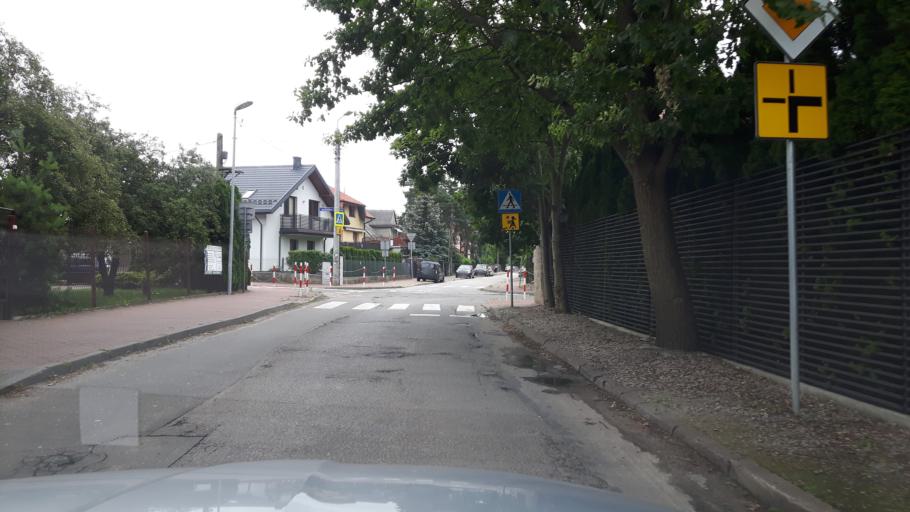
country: PL
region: Masovian Voivodeship
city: Zielonka
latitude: 52.3091
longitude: 21.1587
